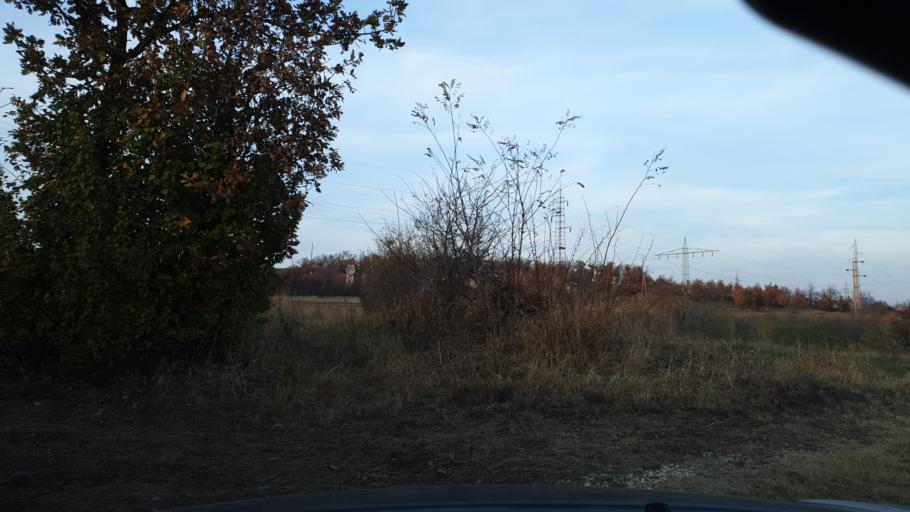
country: RS
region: Central Serbia
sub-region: Borski Okrug
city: Bor
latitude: 44.0622
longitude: 22.0898
